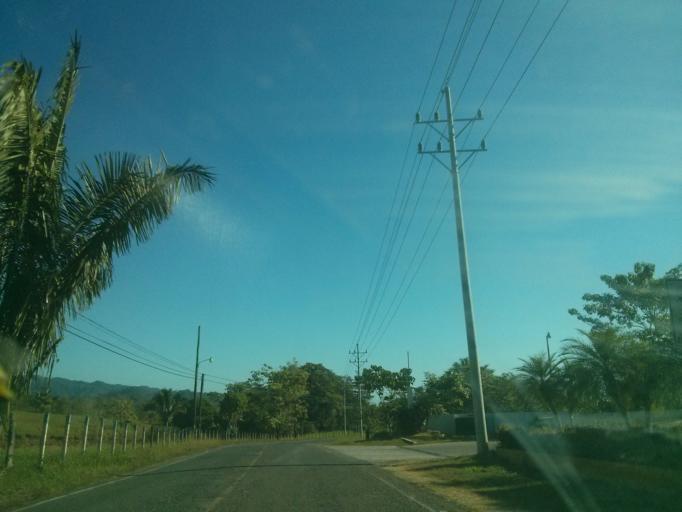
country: CR
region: Puntarenas
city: Paquera
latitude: 9.6942
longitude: -85.0960
